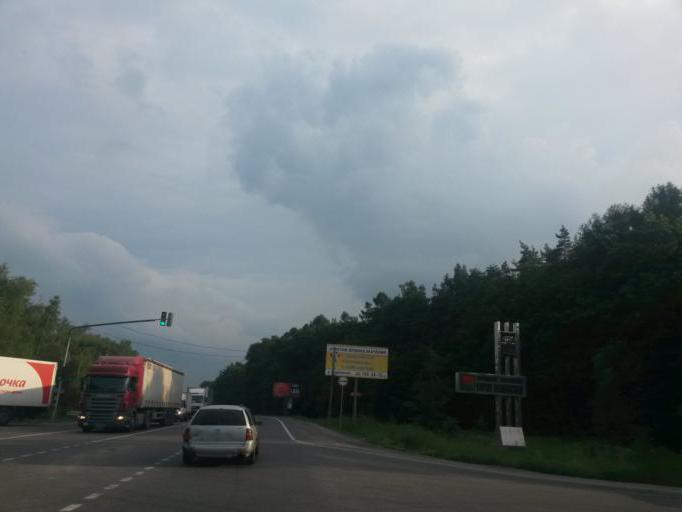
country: RU
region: Moskovskaya
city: Petrovskaya
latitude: 55.5325
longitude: 37.7679
